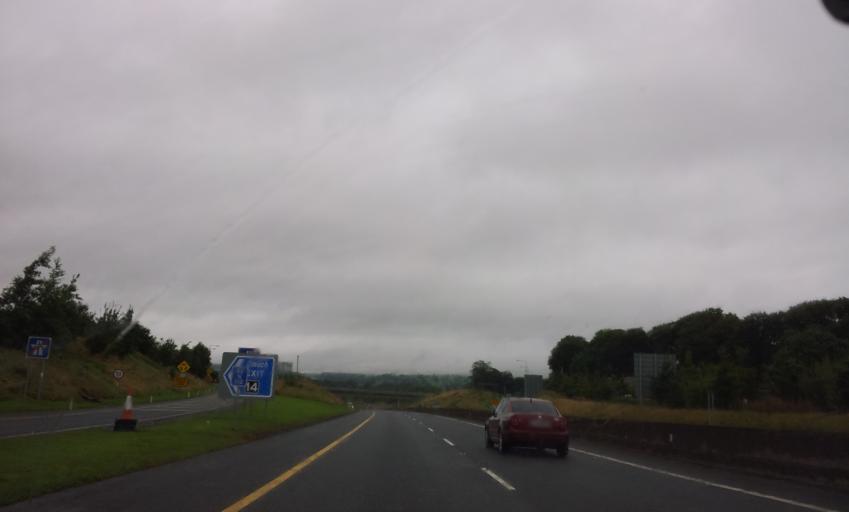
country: IE
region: Munster
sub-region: County Cork
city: Fermoy
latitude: 52.1588
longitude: -8.2658
